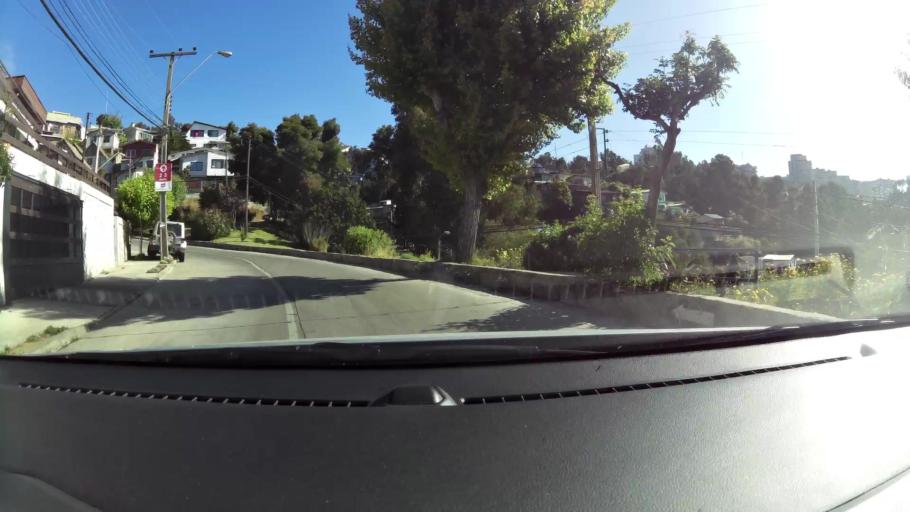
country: CL
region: Valparaiso
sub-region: Provincia de Valparaiso
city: Vina del Mar
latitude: -33.0343
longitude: -71.5605
